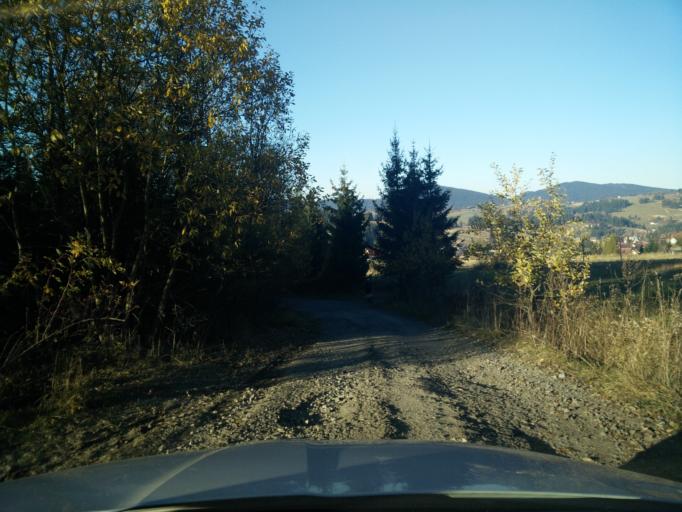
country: SK
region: Zilinsky
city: Oravska Lesna
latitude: 49.3556
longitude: 19.1535
